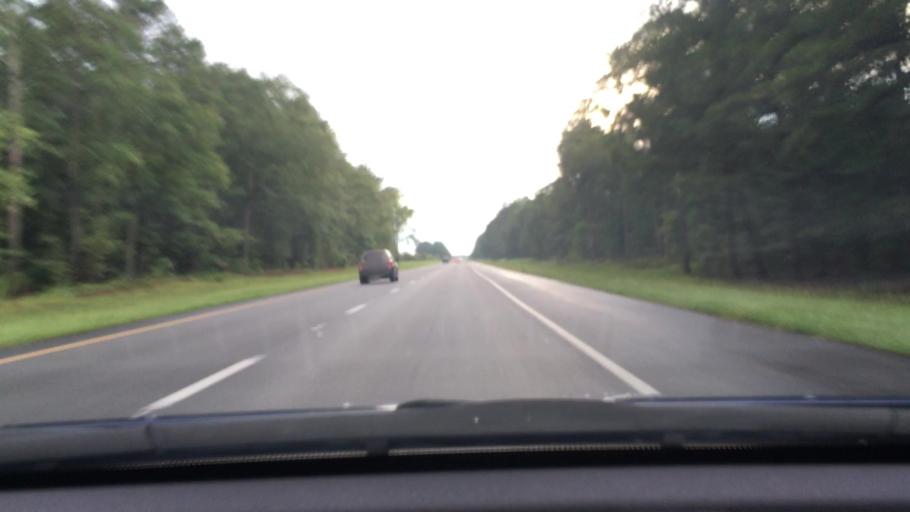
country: US
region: South Carolina
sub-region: Lee County
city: Bishopville
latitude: 34.1960
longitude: -80.3014
